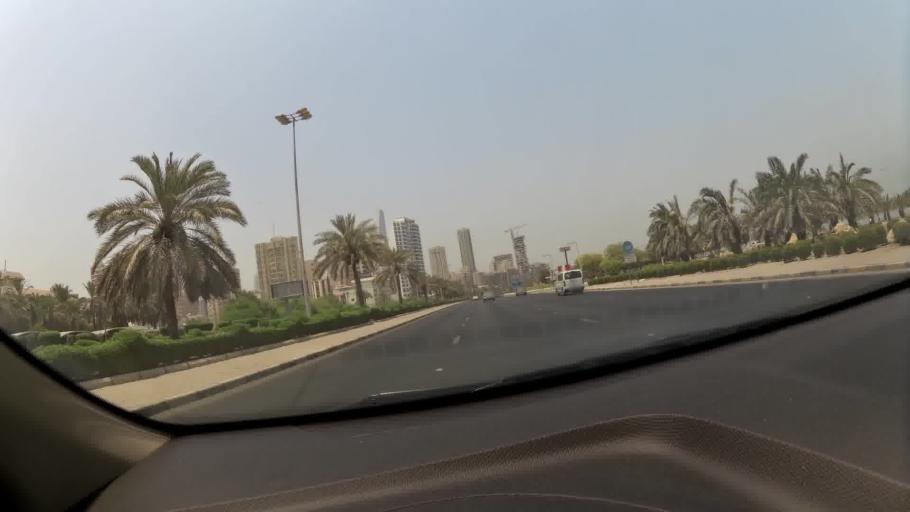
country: KW
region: Al Asimah
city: Ad Dasmah
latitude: 29.3715
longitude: 48.0091
